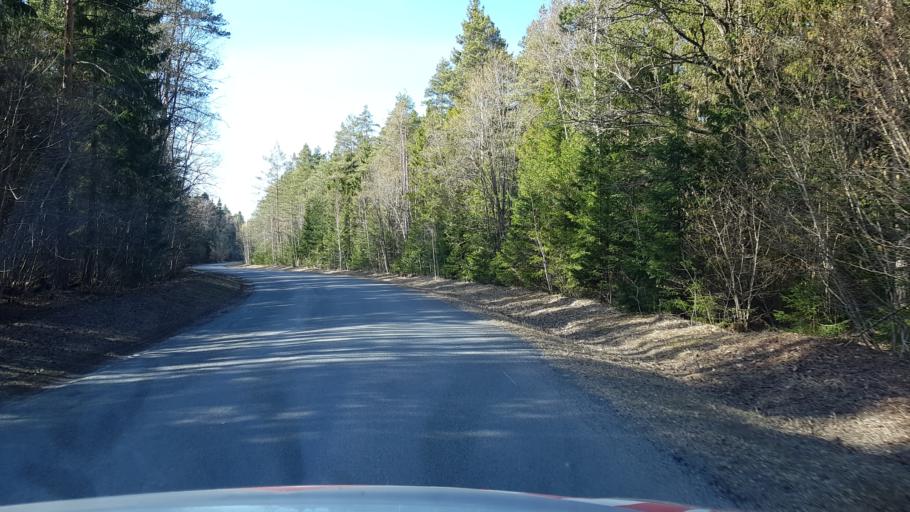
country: EE
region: Harju
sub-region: Nissi vald
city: Riisipere
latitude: 59.0888
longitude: 24.3503
